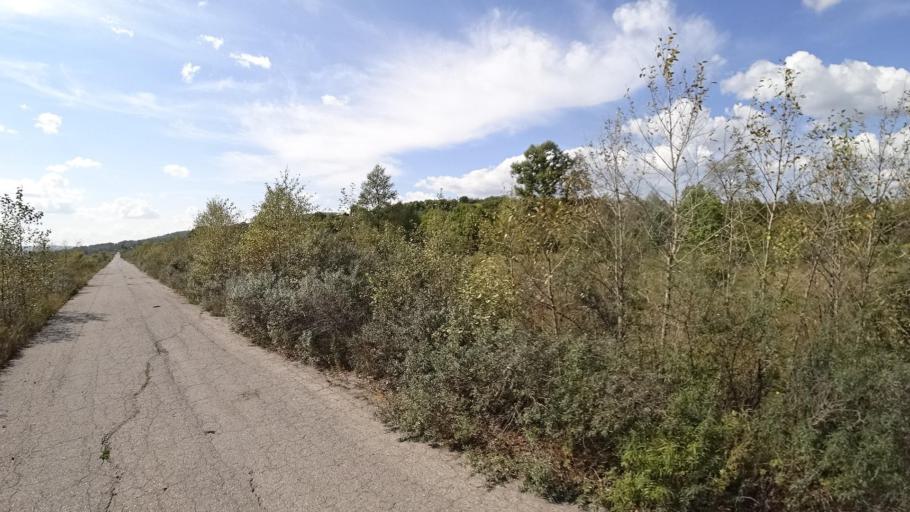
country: RU
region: Jewish Autonomous Oblast
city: Londoko
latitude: 49.0040
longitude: 131.8727
